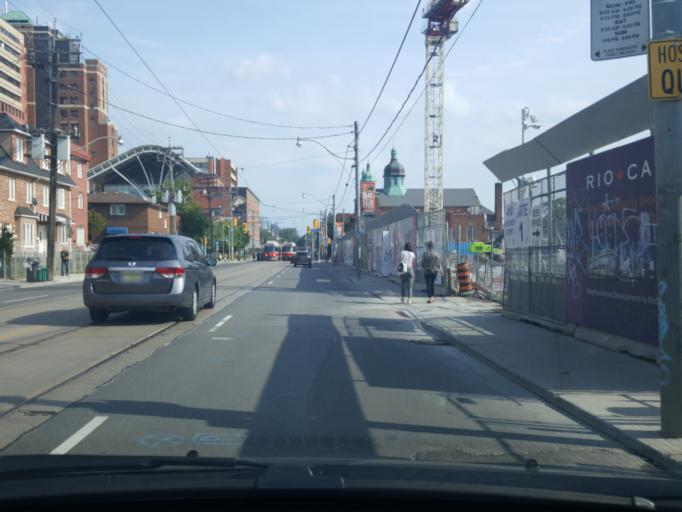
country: CA
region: Ontario
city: Toronto
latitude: 43.6552
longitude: -79.4072
